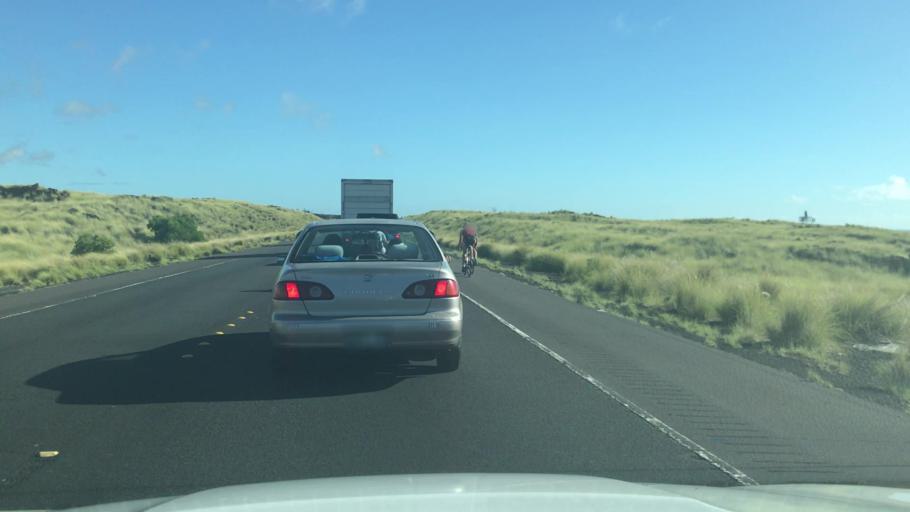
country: US
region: Hawaii
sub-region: Hawaii County
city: Kalaoa
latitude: 19.7541
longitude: -156.0268
